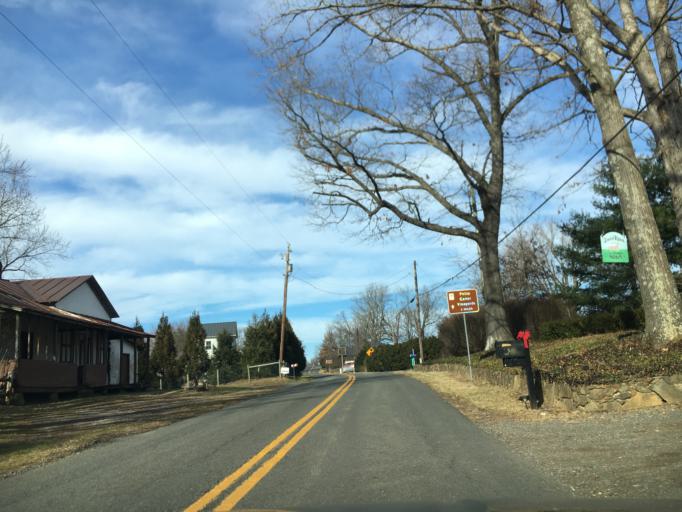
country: US
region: Virginia
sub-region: Warren County
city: Apple Mountain Lake
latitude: 38.8299
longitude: -77.9989
